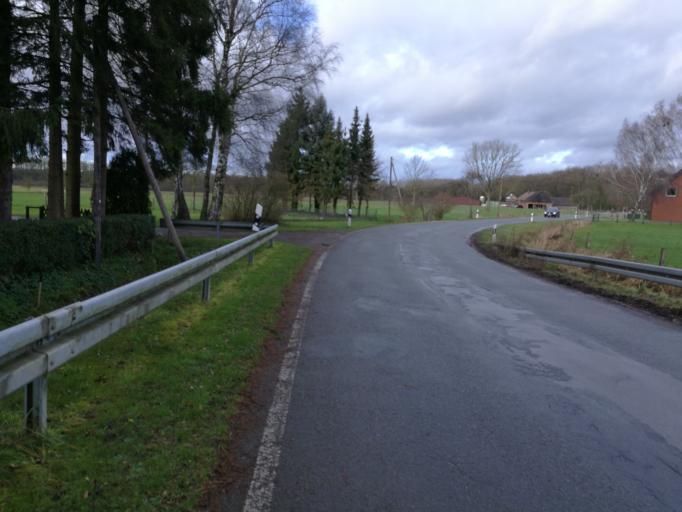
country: DE
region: North Rhine-Westphalia
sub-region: Regierungsbezirk Munster
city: Beckum
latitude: 51.6902
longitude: 8.1145
